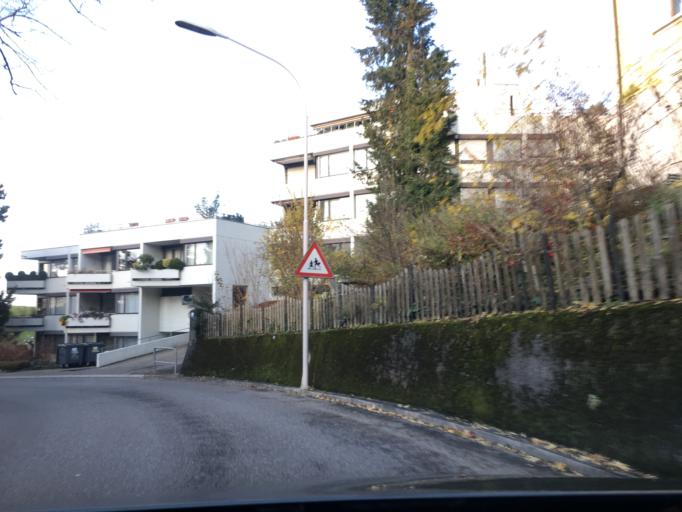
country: CH
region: Zurich
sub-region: Bezirk Zuerich
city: Zuerich (Kreis 6) / Oberstrass
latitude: 47.3922
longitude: 8.5510
